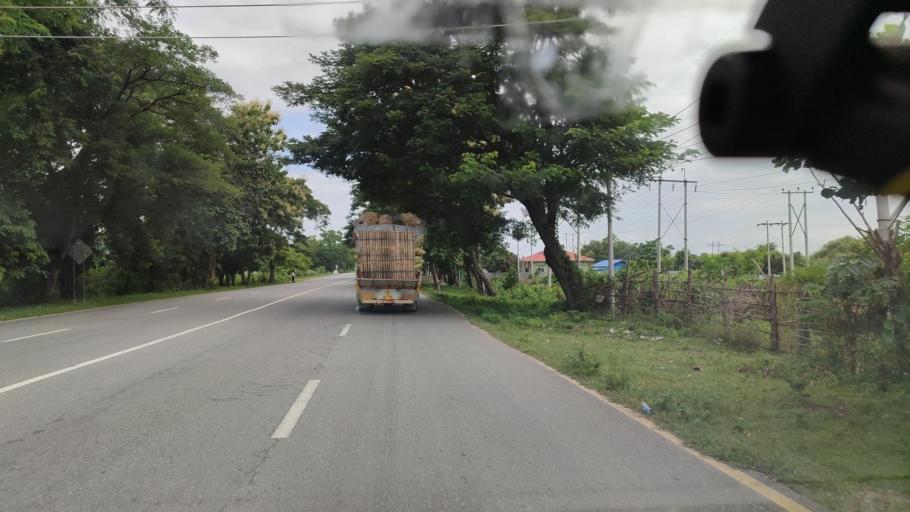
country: MM
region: Mandalay
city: Pyinmana
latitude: 20.0171
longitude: 96.2471
